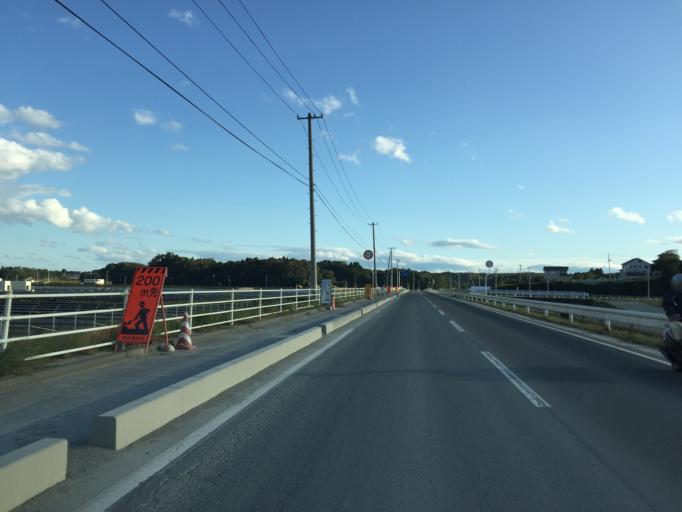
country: JP
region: Miyagi
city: Marumori
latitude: 37.7704
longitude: 140.9818
